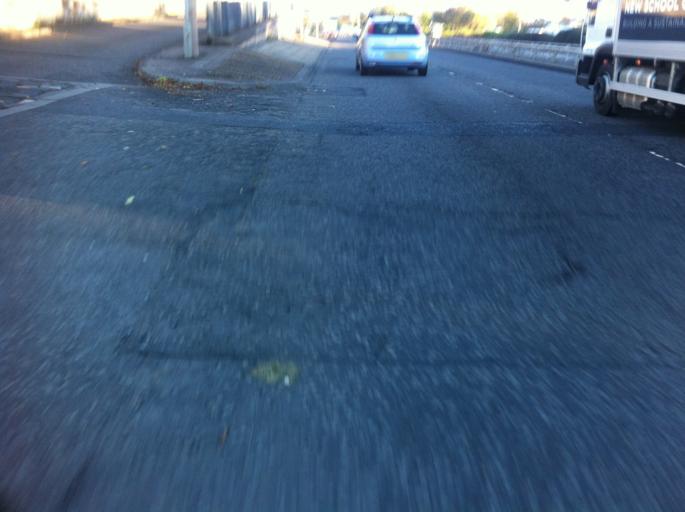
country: GB
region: Scotland
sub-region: Glasgow City
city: Glasgow
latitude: 55.8754
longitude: -4.2326
